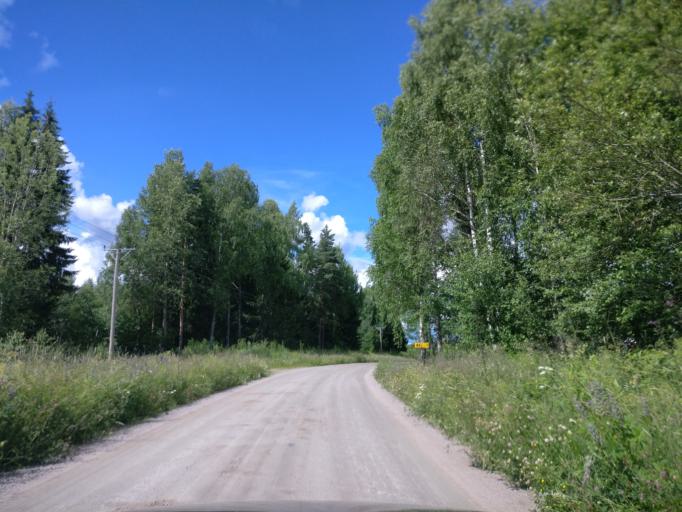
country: SE
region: Vaermland
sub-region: Hagfors Kommun
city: Hagfors
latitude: 60.0330
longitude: 13.6675
